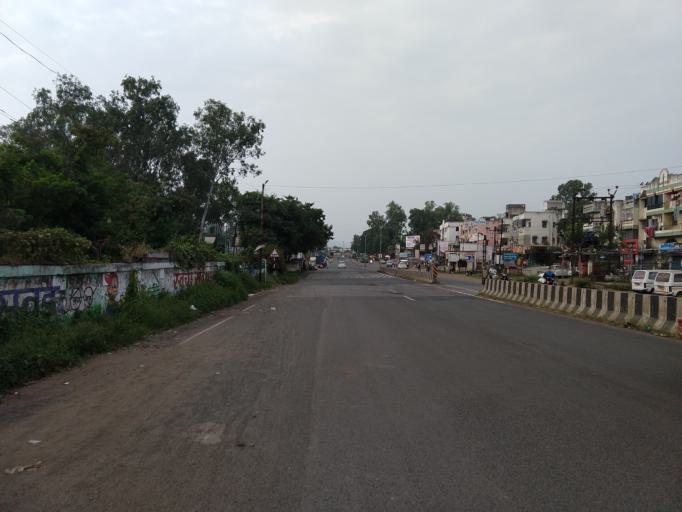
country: IN
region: Maharashtra
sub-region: Pune Division
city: Sasvad
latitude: 18.3514
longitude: 74.0288
